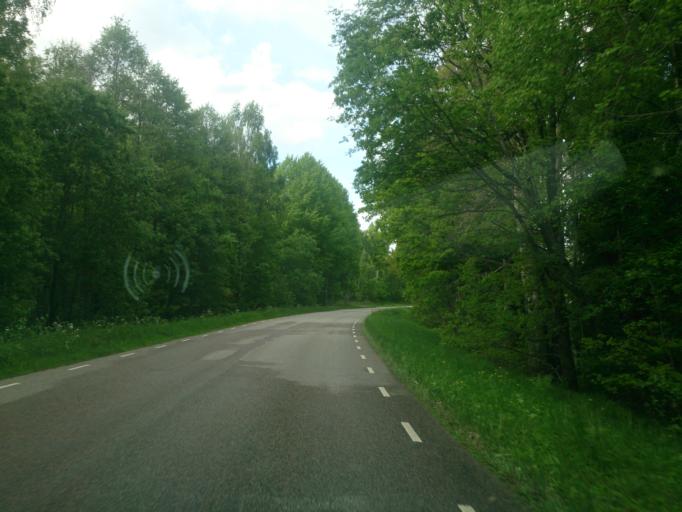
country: SE
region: OEstergoetland
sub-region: Atvidabergs Kommun
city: Atvidaberg
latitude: 58.2398
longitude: 16.0052
